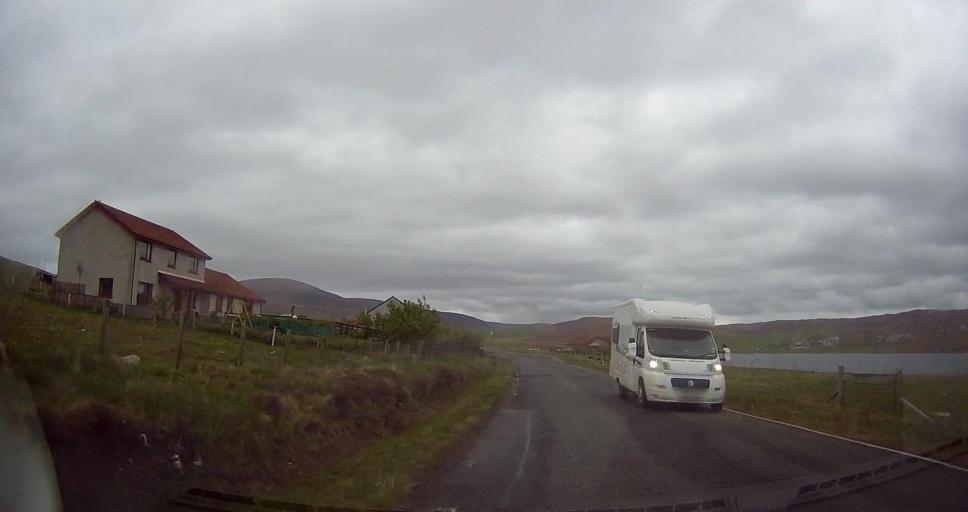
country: GB
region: Scotland
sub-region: Shetland Islands
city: Lerwick
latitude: 60.4844
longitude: -1.4706
